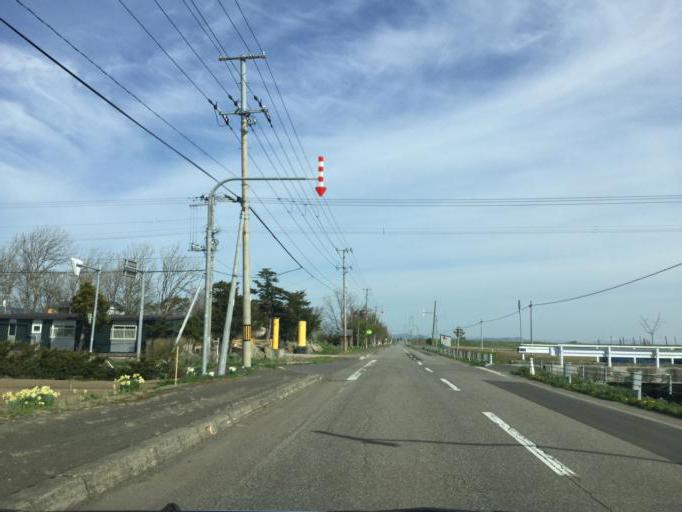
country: JP
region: Hokkaido
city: Iwamizawa
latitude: 43.1250
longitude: 141.6898
